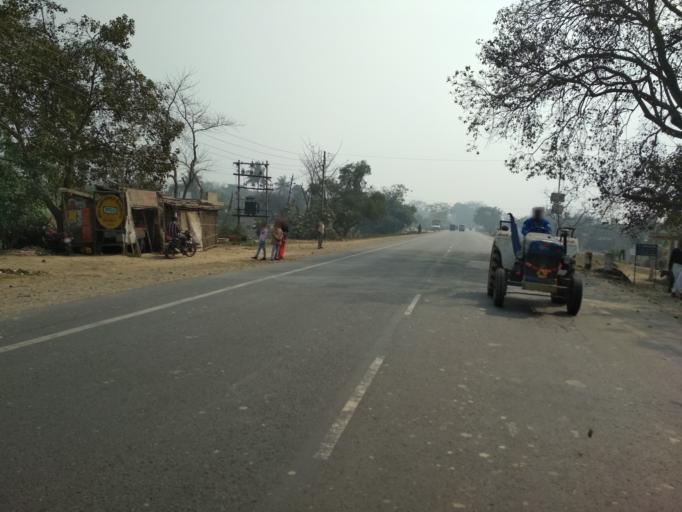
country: IN
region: Bihar
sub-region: Khagaria
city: Khagaria
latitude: 25.5018
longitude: 86.5917
